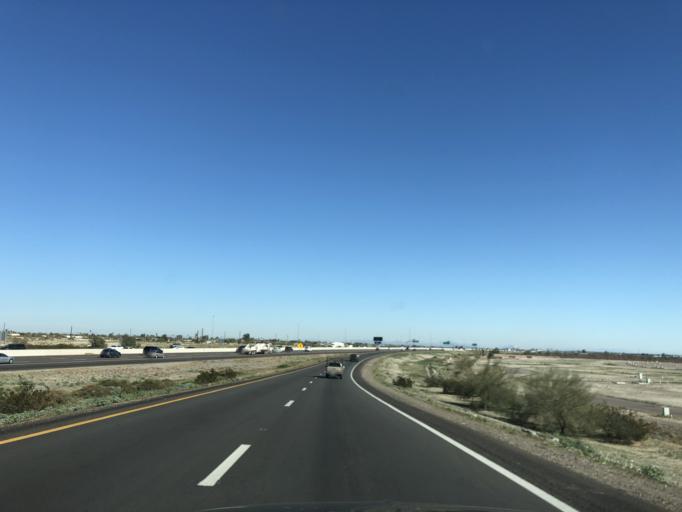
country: US
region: Arizona
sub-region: Maricopa County
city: Citrus Park
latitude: 33.4610
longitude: -112.5028
